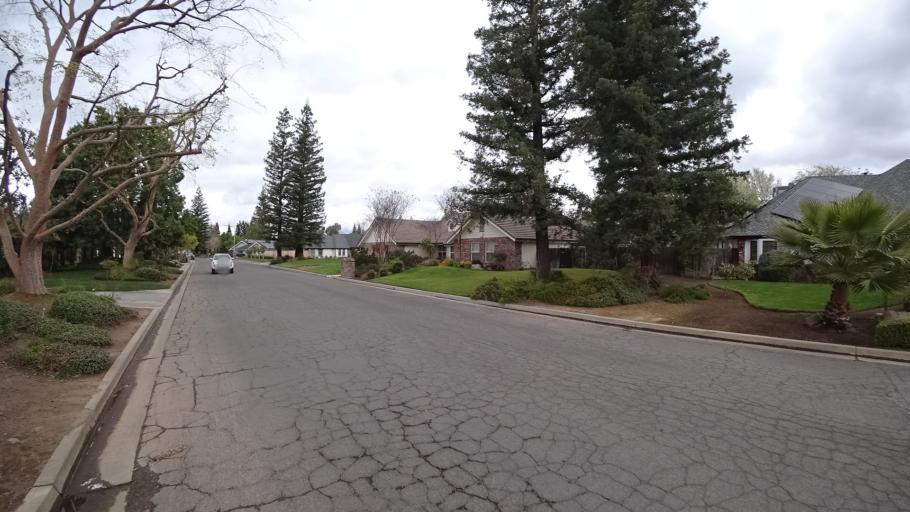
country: US
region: California
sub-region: Fresno County
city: Fresno
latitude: 36.8414
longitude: -119.8295
